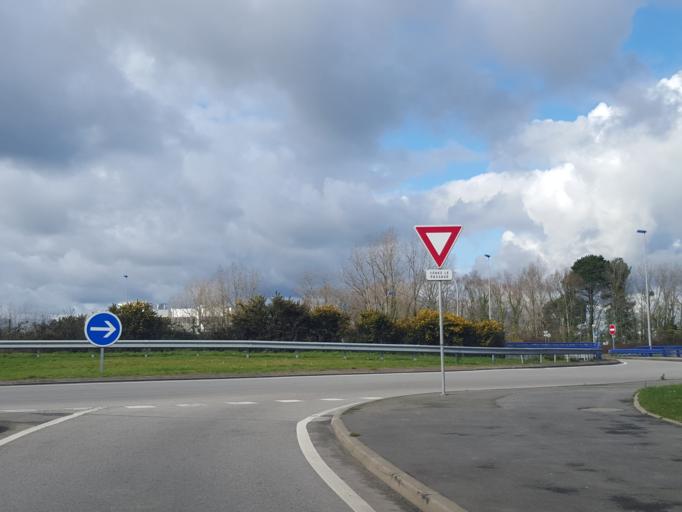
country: FR
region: Pays de la Loire
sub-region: Departement de la Vendee
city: La Roche-sur-Yon
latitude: 46.6834
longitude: -1.4468
